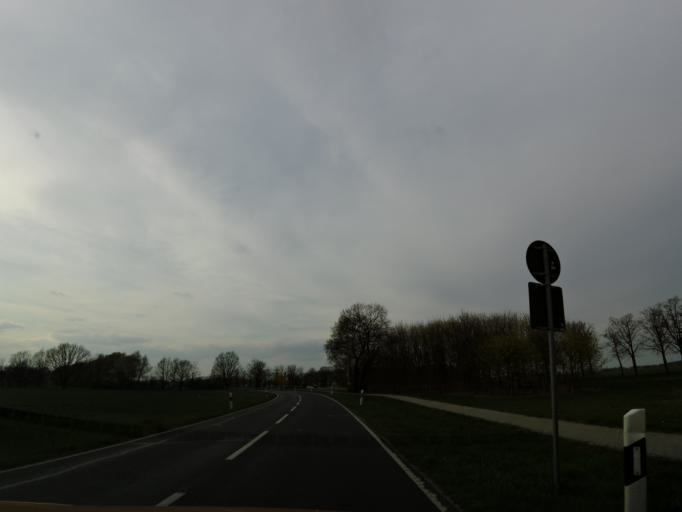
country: DE
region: Brandenburg
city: Mittenwalde
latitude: 52.3035
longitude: 13.5151
